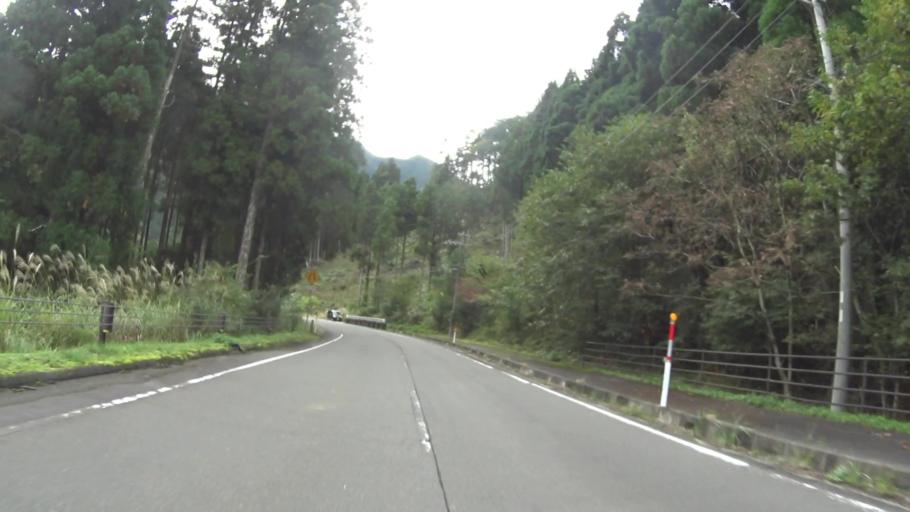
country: JP
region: Fukui
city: Obama
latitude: 35.3233
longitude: 135.6686
